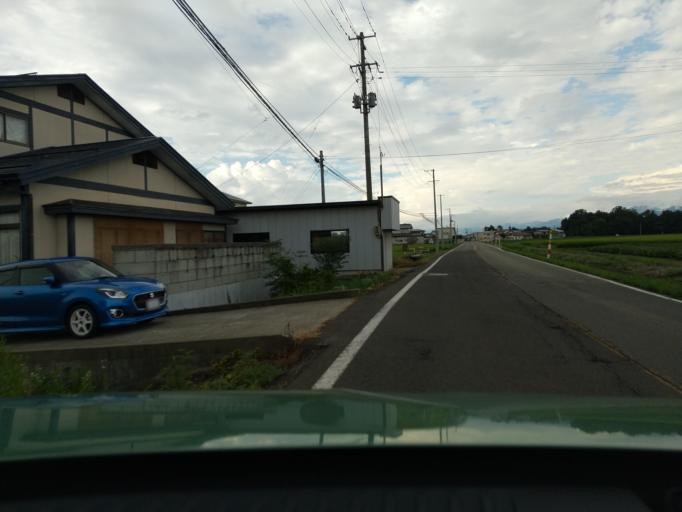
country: JP
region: Akita
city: Yokotemachi
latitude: 39.3298
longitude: 140.4856
